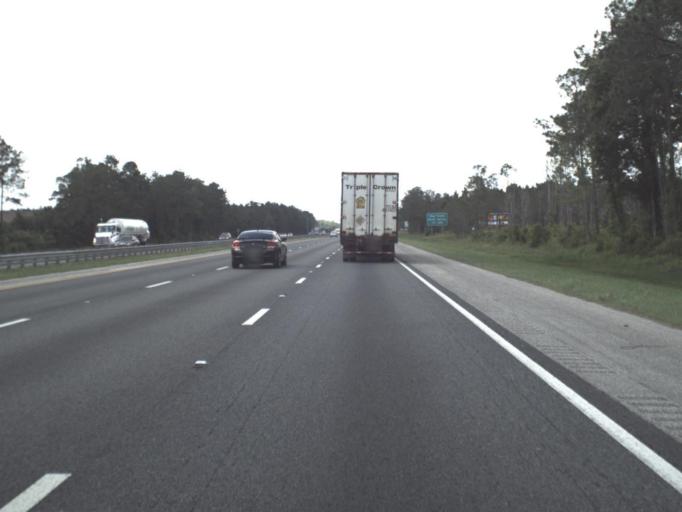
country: US
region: Florida
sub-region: Saint Johns County
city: Fruit Cove
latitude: 30.0524
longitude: -81.4972
